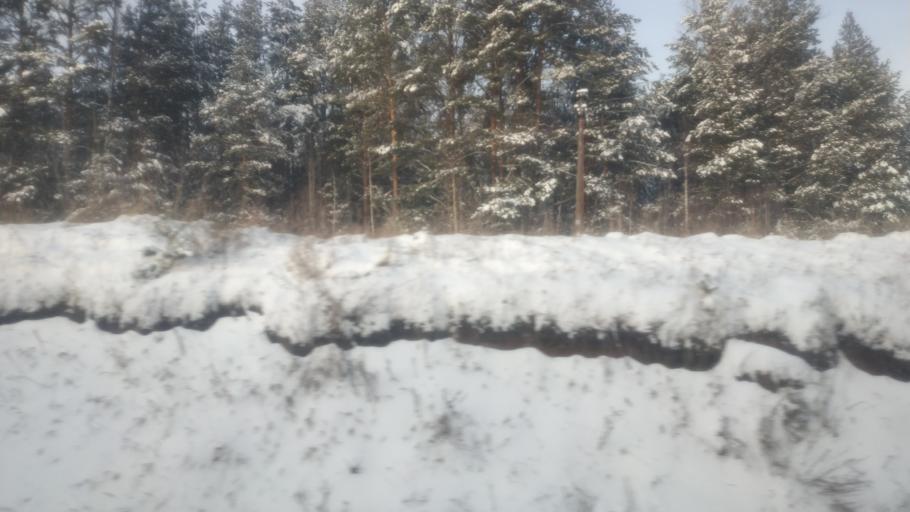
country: RU
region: Kirov
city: Krasnaya Polyana
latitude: 56.2496
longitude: 51.2105
